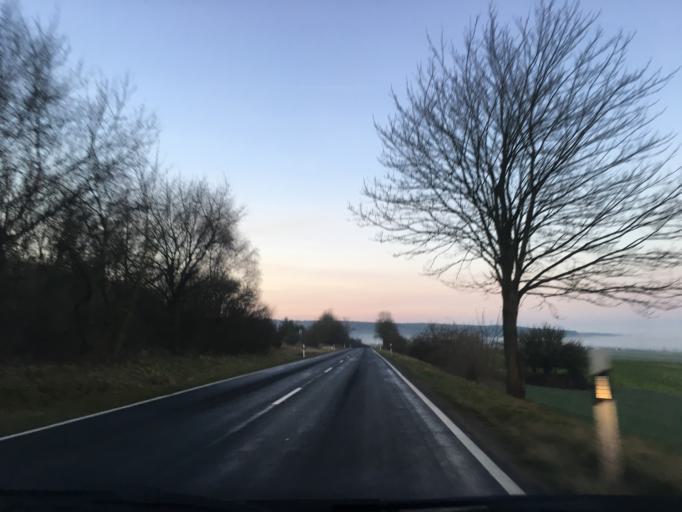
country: DE
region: Hesse
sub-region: Regierungsbezirk Kassel
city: Hofbieber
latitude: 50.5879
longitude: 9.8216
